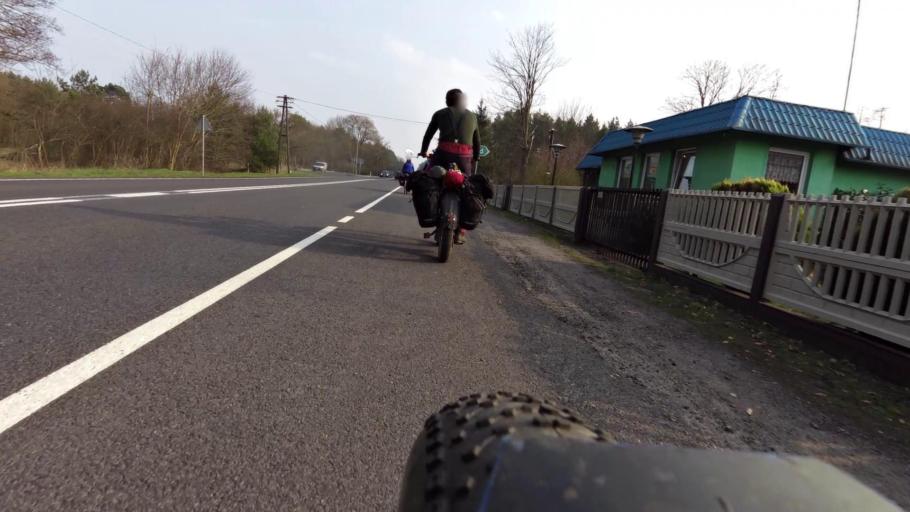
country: PL
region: Lubusz
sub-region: Powiat slubicki
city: Cybinka
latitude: 52.2489
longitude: 14.7326
